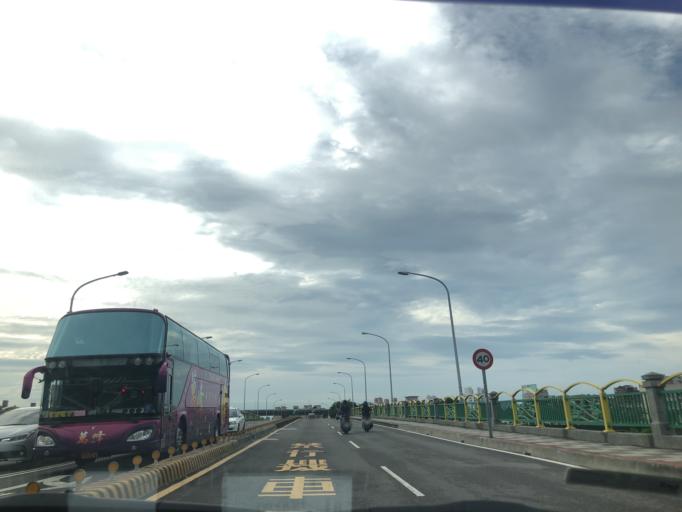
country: TW
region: Taiwan
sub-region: Taichung City
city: Taichung
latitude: 24.0970
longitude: 120.6953
